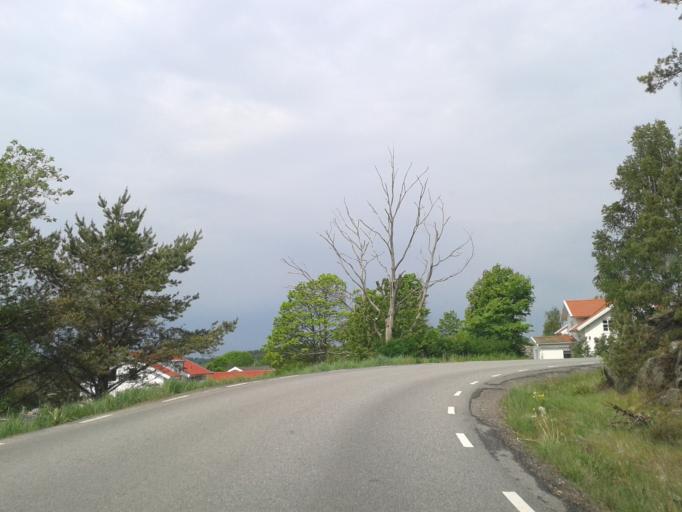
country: SE
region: Vaestra Goetaland
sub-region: Kungalvs Kommun
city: Kungalv
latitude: 57.9071
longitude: 11.9390
